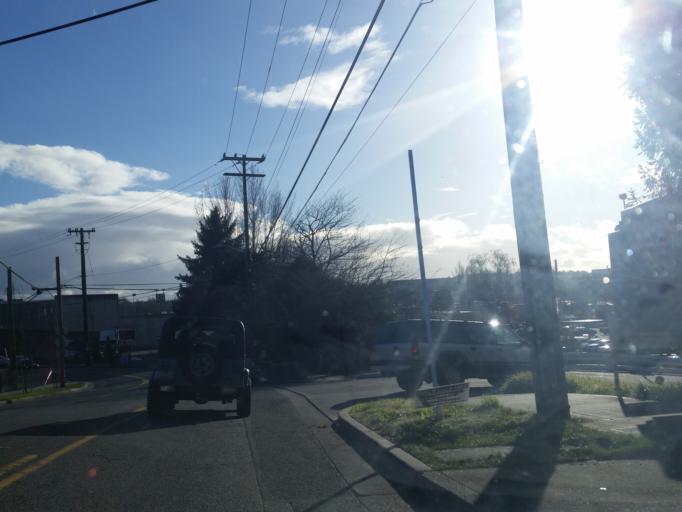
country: US
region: Washington
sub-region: King County
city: Seattle
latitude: 47.6644
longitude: -122.2957
